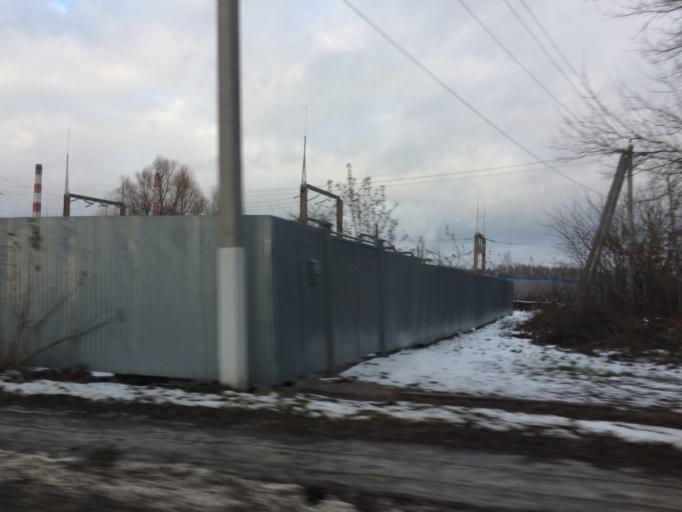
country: RU
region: Tula
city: Suvorov
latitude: 54.1270
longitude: 36.4832
